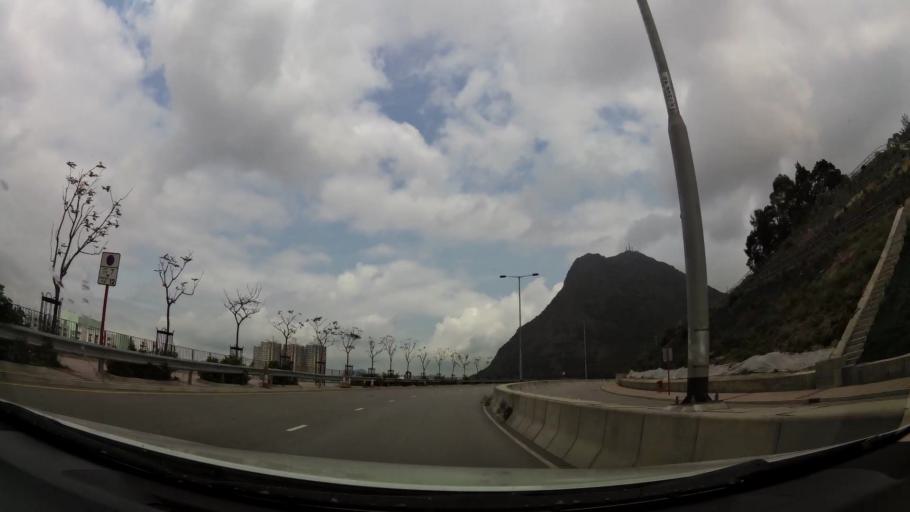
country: HK
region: Kowloon City
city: Kowloon
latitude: 22.3296
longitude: 114.2288
